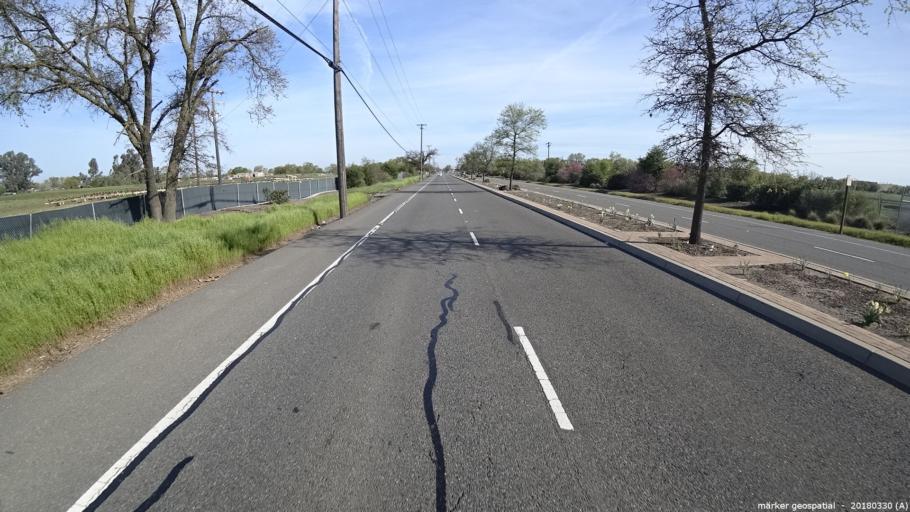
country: US
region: California
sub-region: Sacramento County
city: Rosemont
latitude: 38.5213
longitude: -121.3350
